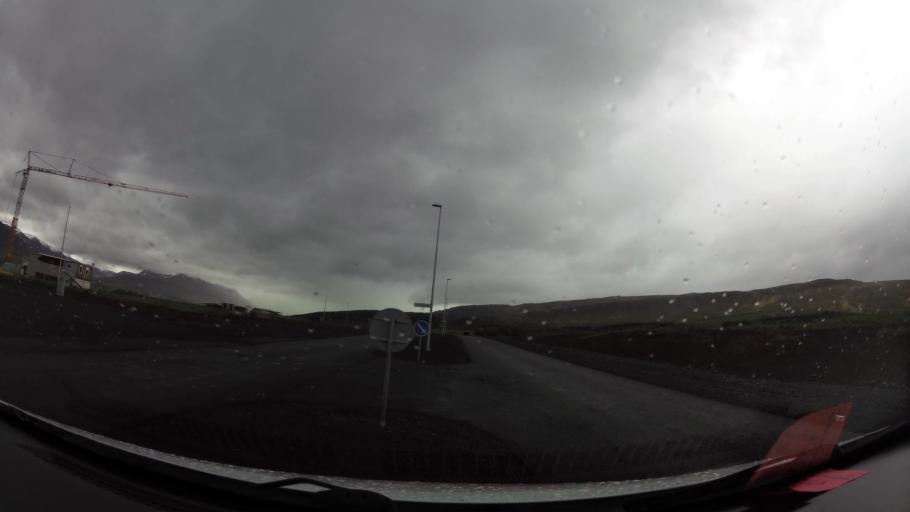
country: IS
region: Northeast
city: Akureyri
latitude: 65.6609
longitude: -18.0997
